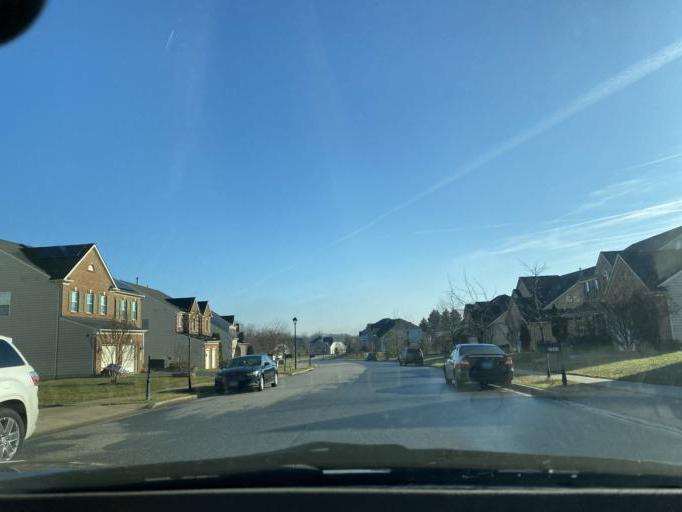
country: US
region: Maryland
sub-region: Prince George's County
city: West Laurel
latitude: 39.0892
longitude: -76.8809
